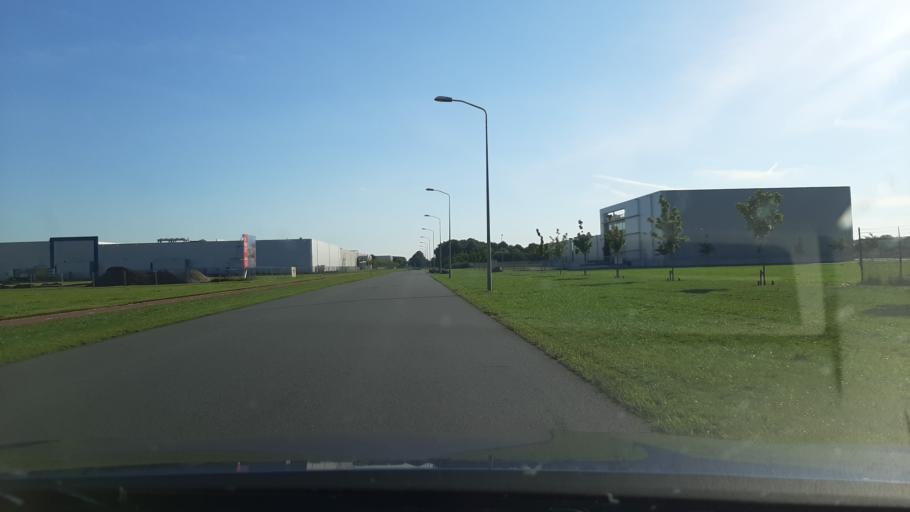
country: NL
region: Flevoland
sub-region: Gemeente Zeewolde
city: Zeewolde
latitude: 52.3626
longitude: 5.5141
